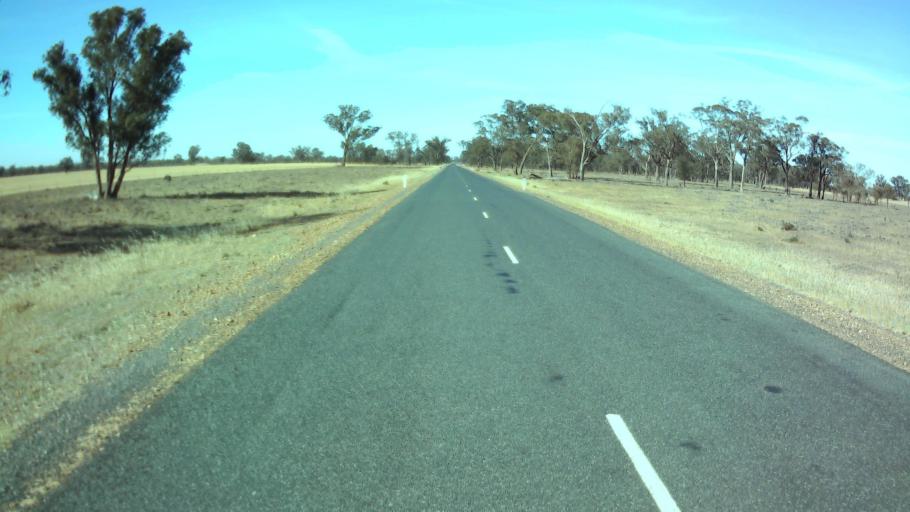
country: AU
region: New South Wales
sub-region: Weddin
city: Grenfell
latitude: -34.0868
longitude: 147.8919
